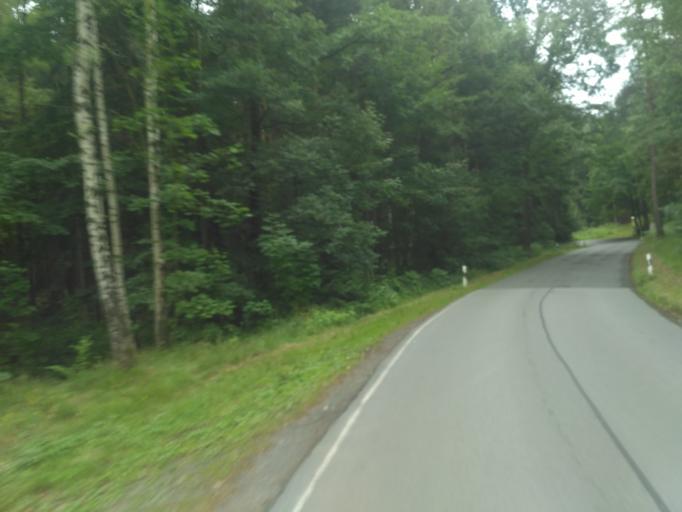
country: DE
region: Saxony
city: Kurort Gohrisch
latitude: 50.9060
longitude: 14.1109
